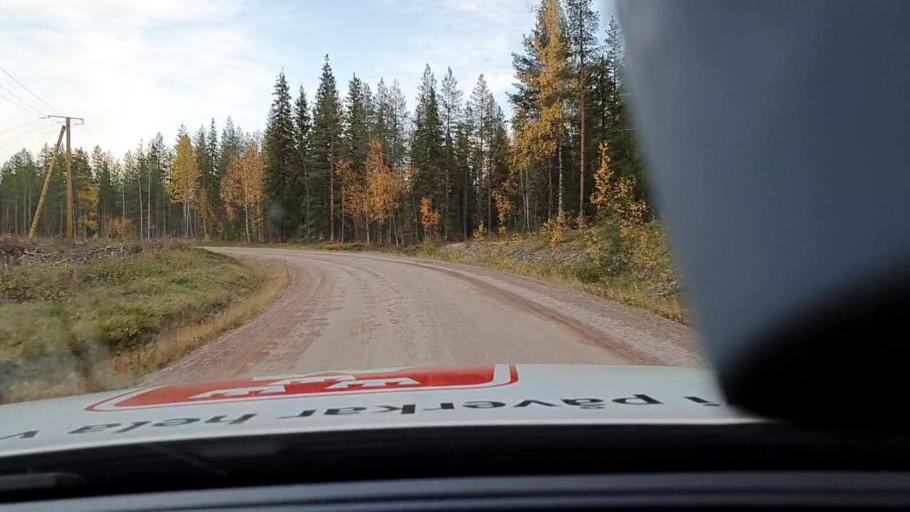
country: SE
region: Norrbotten
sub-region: Overkalix Kommun
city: OEverkalix
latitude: 66.3204
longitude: 22.6368
